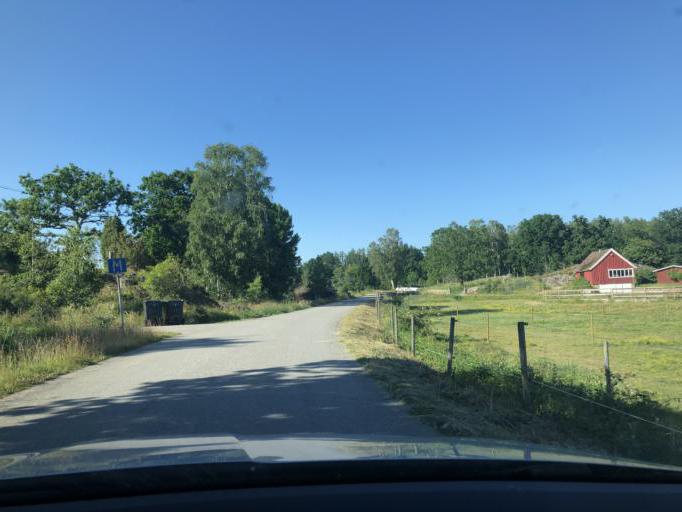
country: SE
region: Blekinge
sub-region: Karlshamns Kommun
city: Morrum
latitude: 56.1590
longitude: 14.7999
